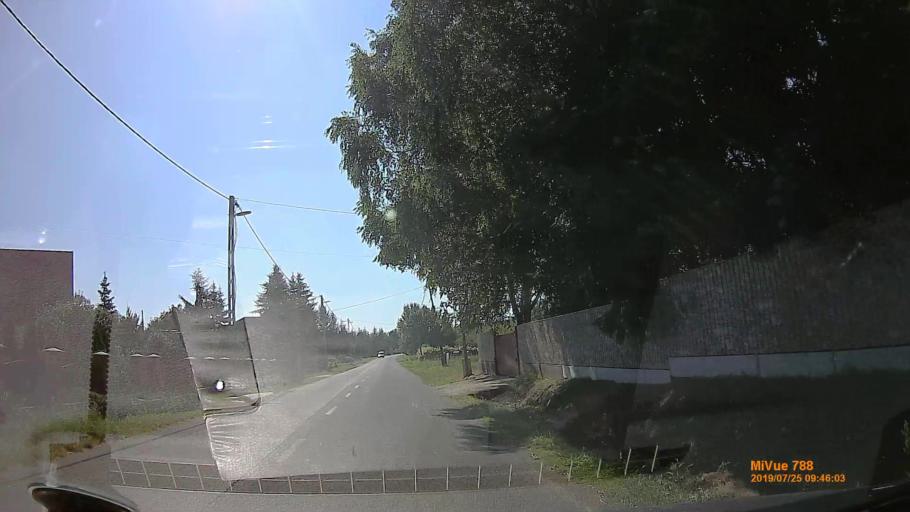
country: HU
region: Szabolcs-Szatmar-Bereg
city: Kotaj
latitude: 48.0334
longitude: 21.7512
